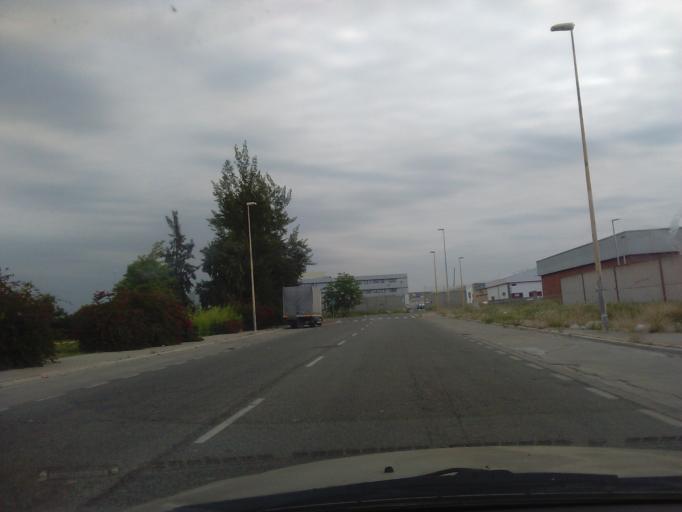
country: ES
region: Andalusia
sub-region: Provincia de Sevilla
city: Sevilla
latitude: 37.3793
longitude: -5.9279
